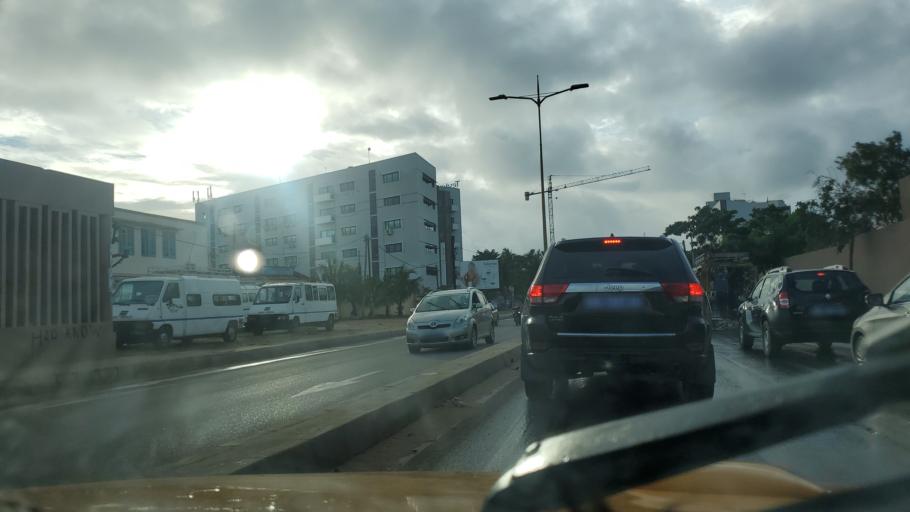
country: SN
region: Dakar
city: Mermoz Boabab
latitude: 14.7161
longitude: -17.4835
